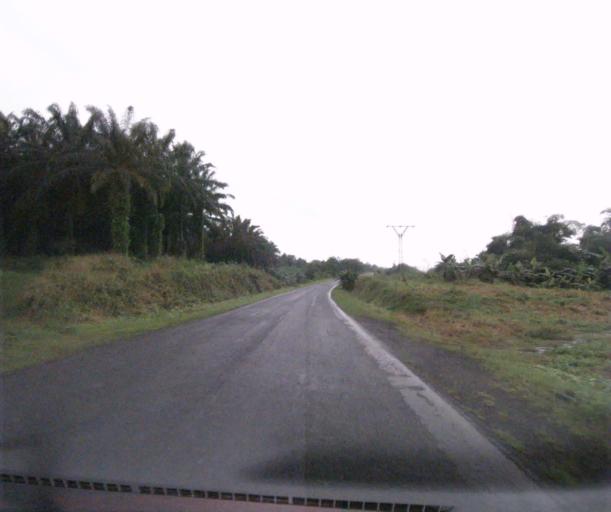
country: CM
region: South-West Province
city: Idenao
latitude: 4.1942
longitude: 9.0032
